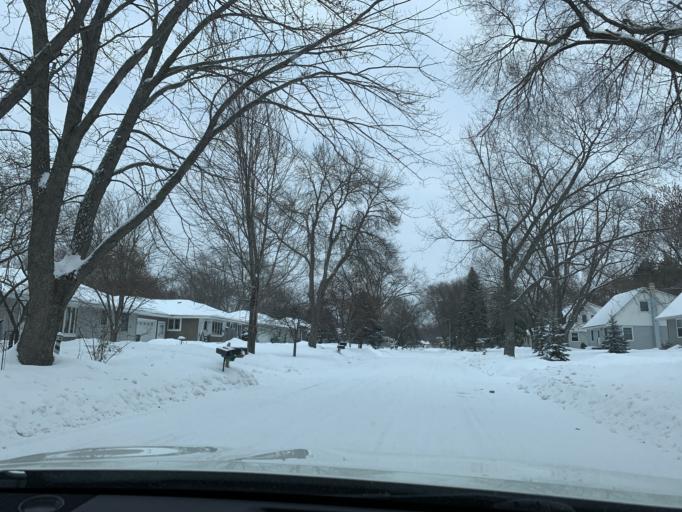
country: US
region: Minnesota
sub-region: Anoka County
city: Coon Rapids
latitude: 45.1736
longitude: -93.2903
